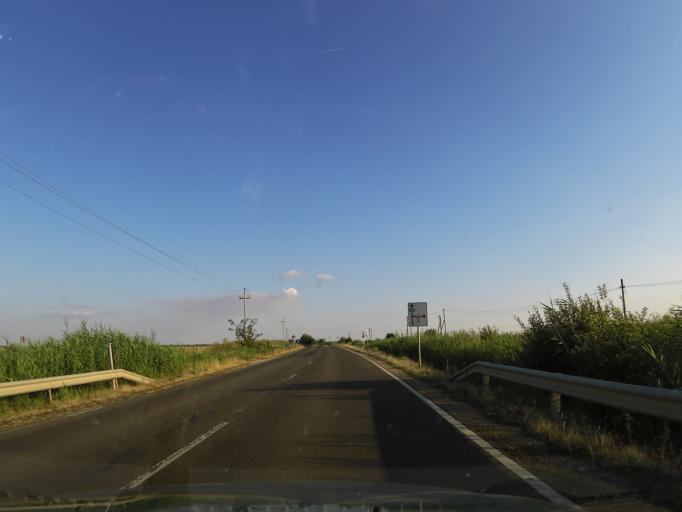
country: HU
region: Jasz-Nagykun-Szolnok
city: Tiszafoldvar
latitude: 46.9374
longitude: 20.2681
